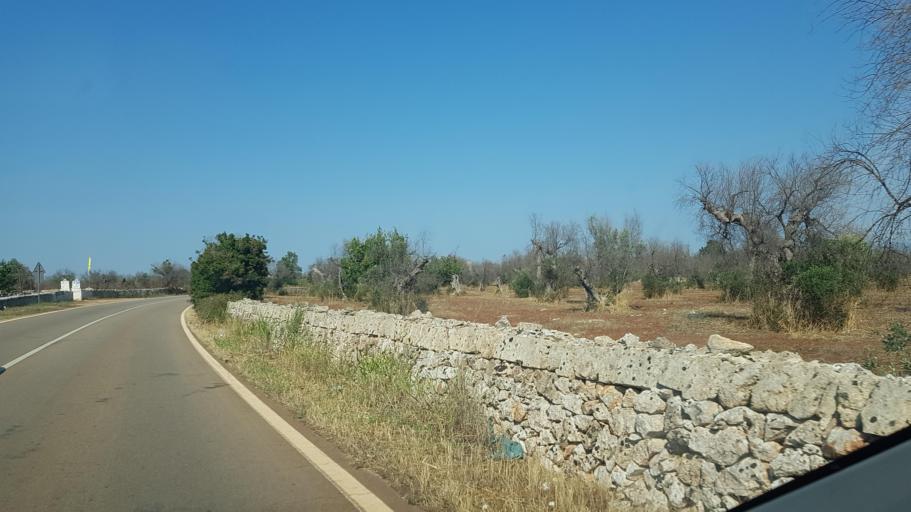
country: IT
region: Apulia
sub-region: Provincia di Lecce
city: Acquarica del Capo
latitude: 39.8899
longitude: 18.2440
